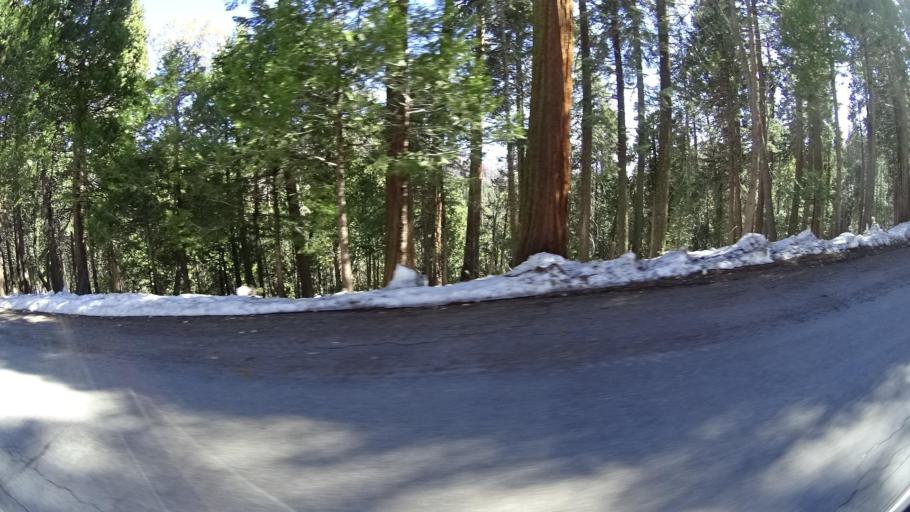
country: US
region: California
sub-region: Kern County
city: Alta Sierra
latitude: 35.7321
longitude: -118.5596
